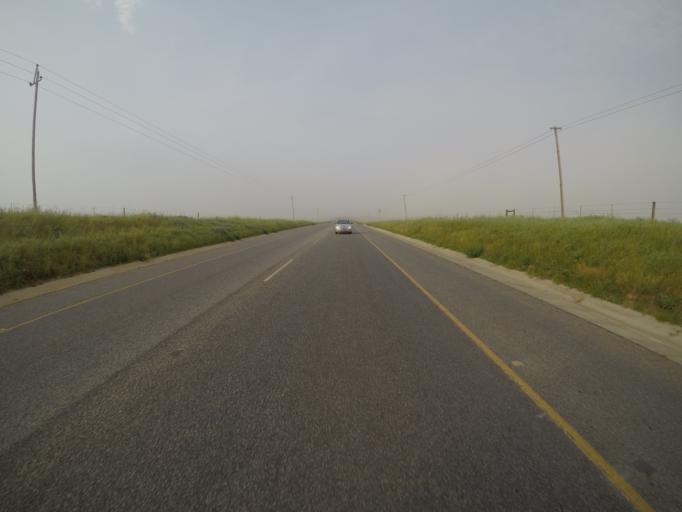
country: ZA
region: Western Cape
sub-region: West Coast District Municipality
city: Malmesbury
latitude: -33.6426
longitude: 18.7151
